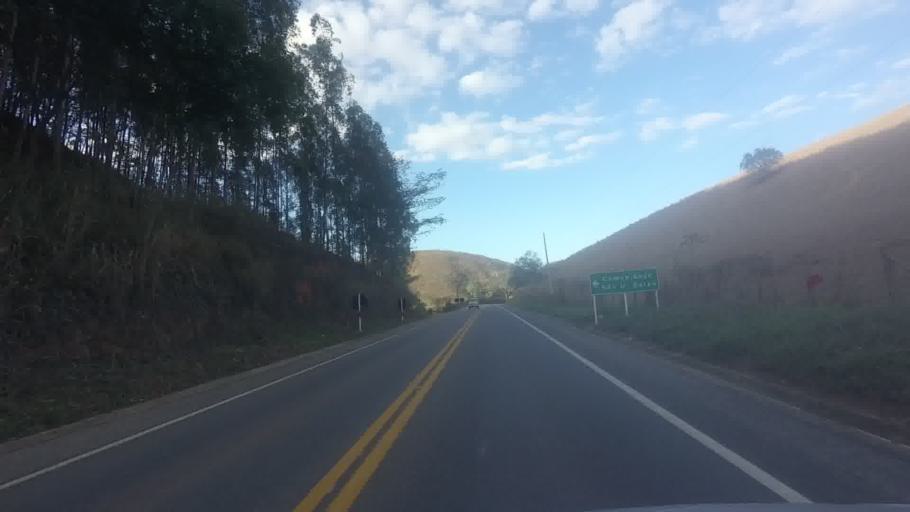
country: BR
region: Espirito Santo
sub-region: Mimoso Do Sul
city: Mimoso do Sul
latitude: -20.9246
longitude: -41.3170
